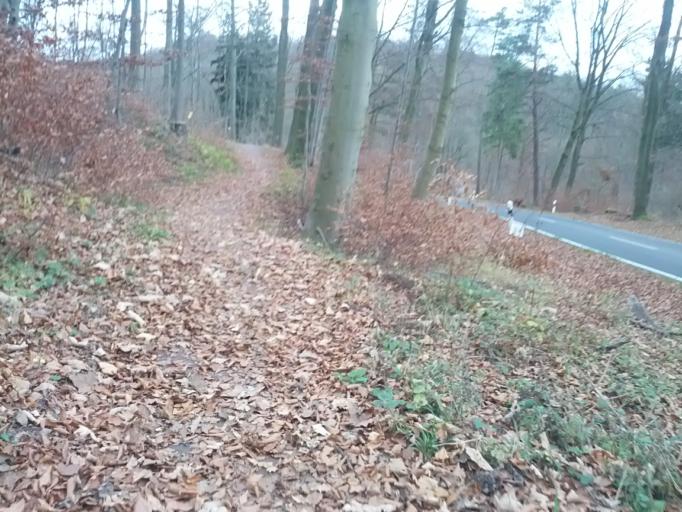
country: DE
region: Thuringia
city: Wolfsburg-Unkeroda
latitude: 50.9538
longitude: 10.2535
